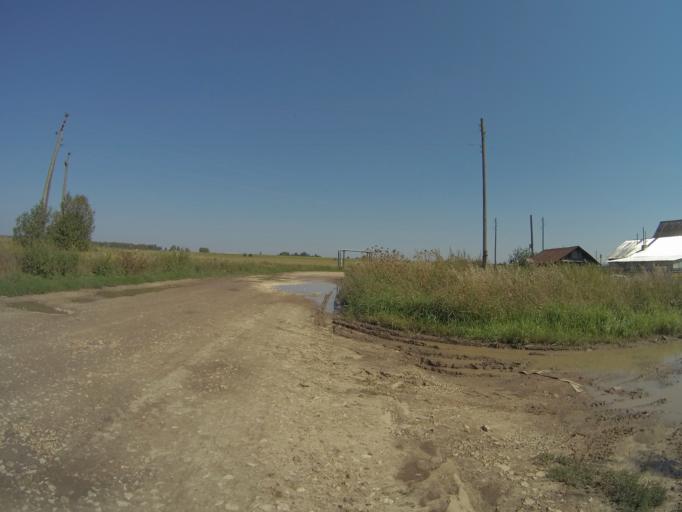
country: RU
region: Vladimir
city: Bogolyubovo
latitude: 56.2414
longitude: 40.5672
